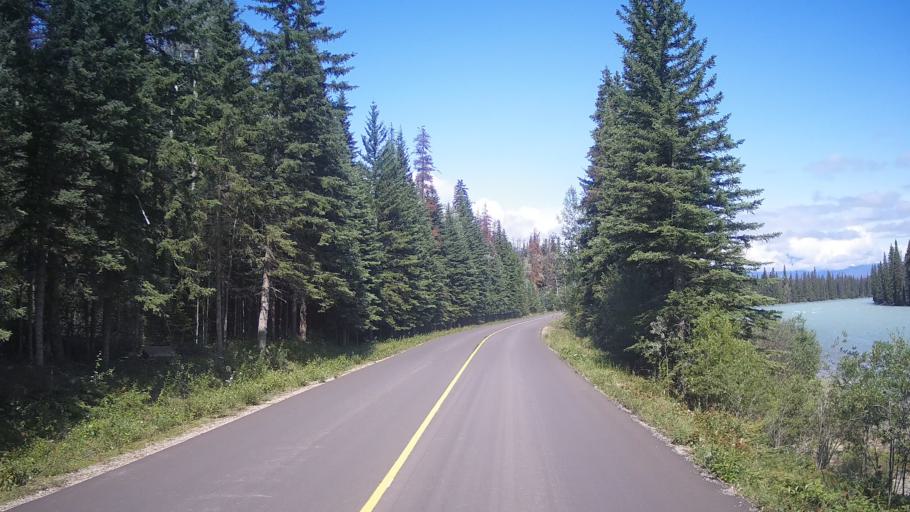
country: CA
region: Alberta
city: Jasper Park Lodge
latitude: 52.7434
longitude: -117.9685
